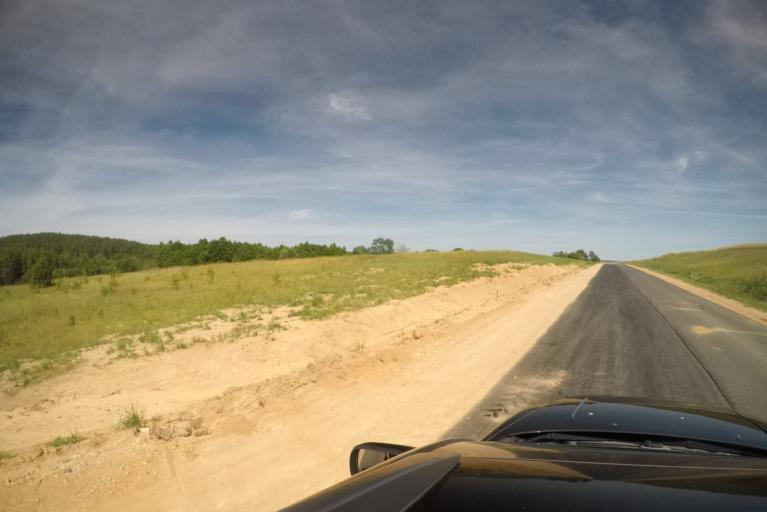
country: BY
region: Grodnenskaya
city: Hal'shany
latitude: 54.2594
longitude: 25.9732
